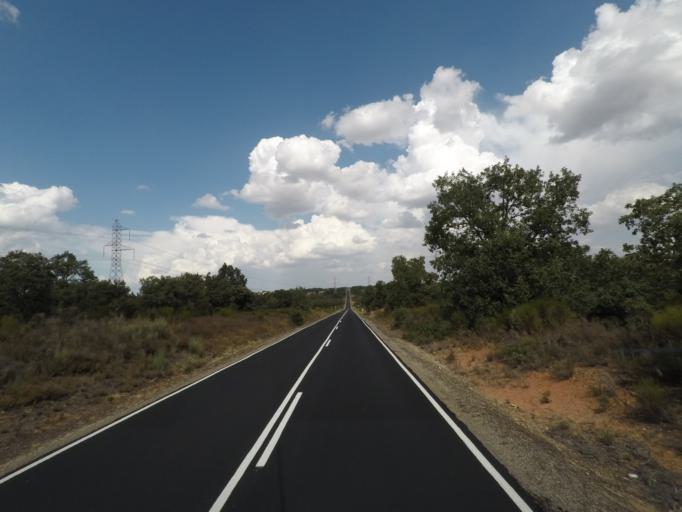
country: ES
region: Castille and Leon
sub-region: Provincia de Zamora
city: Fermoselle
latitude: 41.3076
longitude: -6.3149
